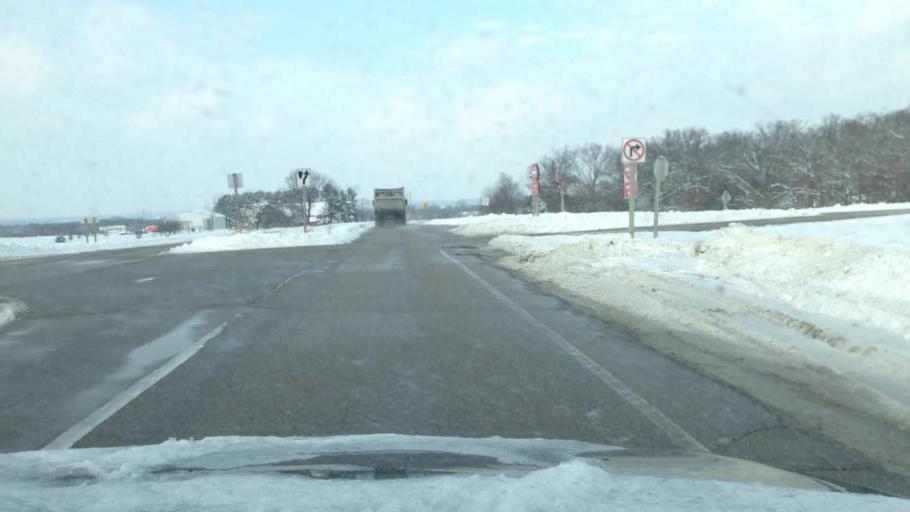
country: US
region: Wisconsin
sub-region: Walworth County
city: East Troy
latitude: 42.7490
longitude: -88.4453
